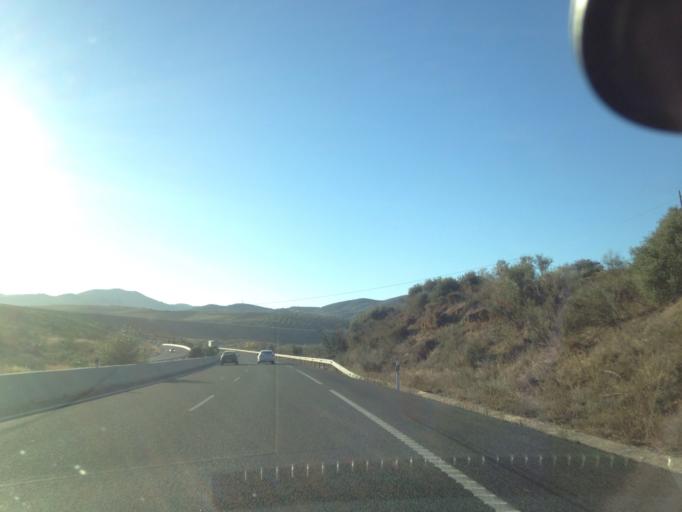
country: ES
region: Andalusia
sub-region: Provincia de Malaga
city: Casabermeja
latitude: 36.9197
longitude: -4.4466
